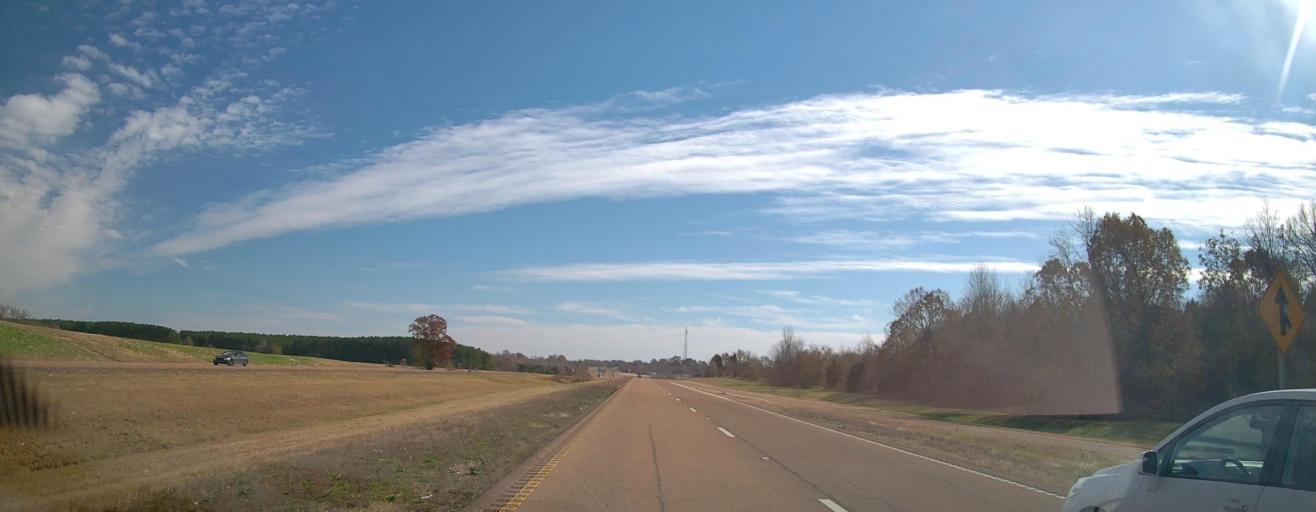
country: US
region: Tennessee
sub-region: Fayette County
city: Piperton
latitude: 34.9650
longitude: -89.5421
